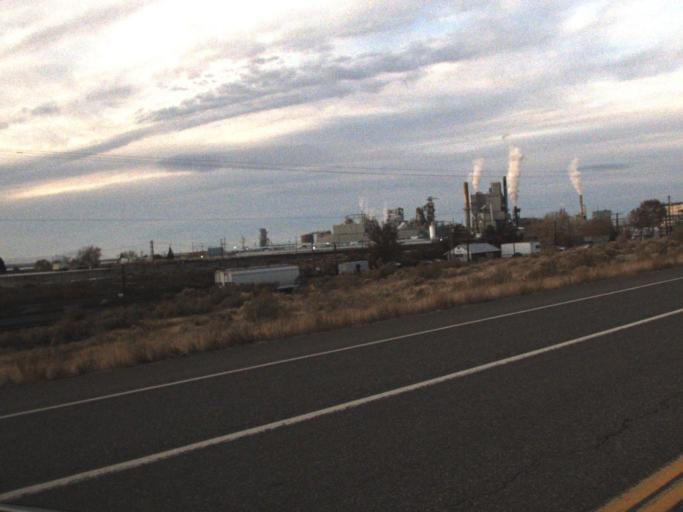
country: US
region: Washington
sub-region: Benton County
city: Finley
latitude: 46.0972
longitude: -118.9121
